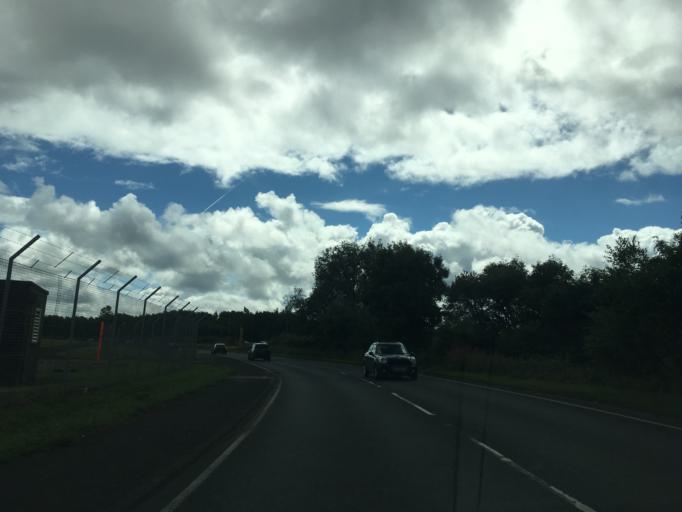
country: GB
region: Scotland
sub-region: Renfrewshire
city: Inchinnan
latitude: 55.8615
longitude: -4.4564
